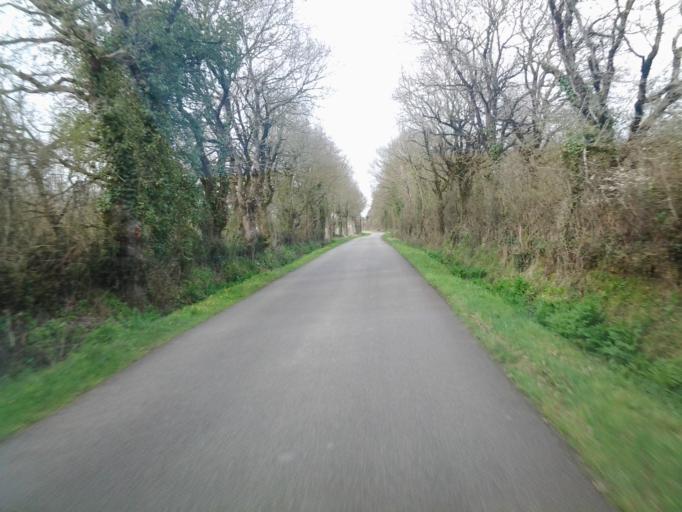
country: FR
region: Pays de la Loire
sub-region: Departement de la Vendee
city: Avrille
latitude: 46.4973
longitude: -1.4665
